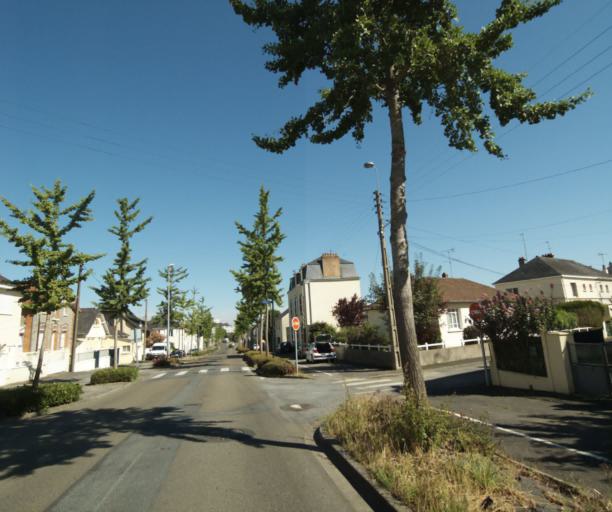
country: FR
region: Pays de la Loire
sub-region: Departement de la Mayenne
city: Laval
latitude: 48.0578
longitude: -0.7521
